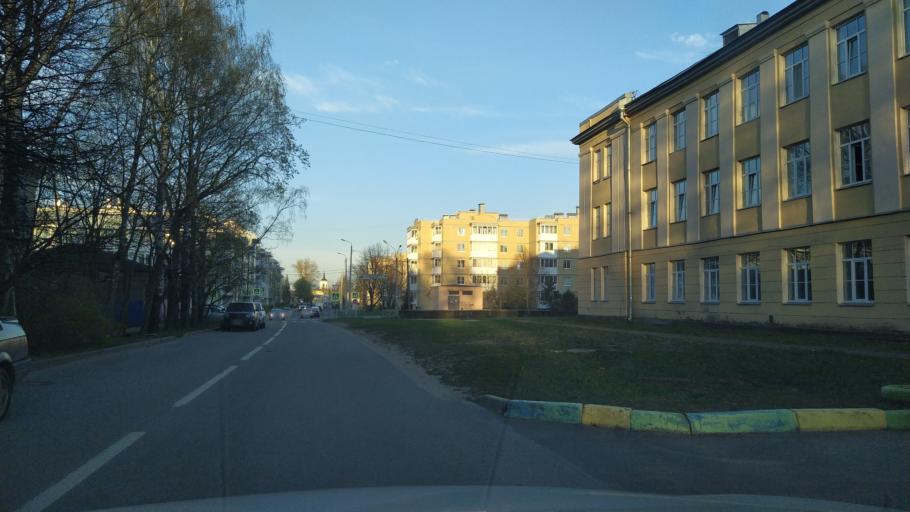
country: RU
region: St.-Petersburg
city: Pushkin
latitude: 59.7075
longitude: 30.3831
